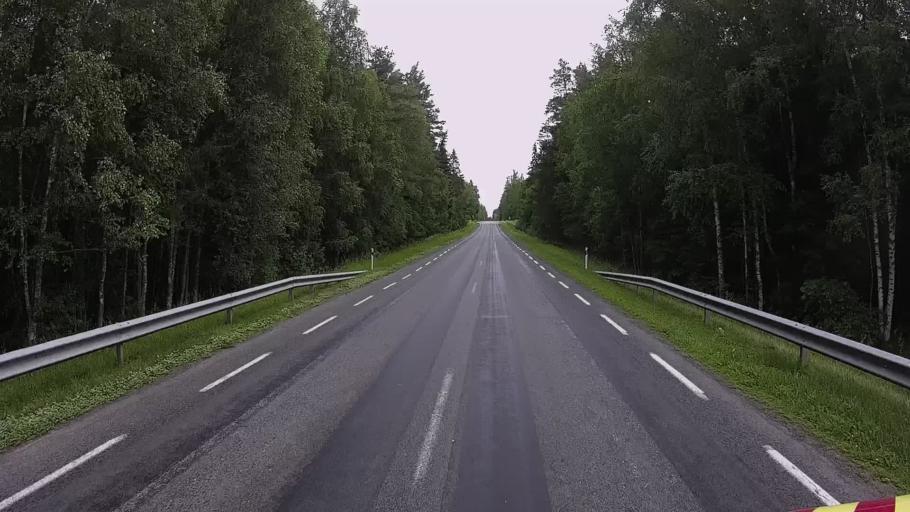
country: EE
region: Viljandimaa
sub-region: Karksi vald
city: Karksi-Nuia
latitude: 58.1854
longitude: 25.5973
